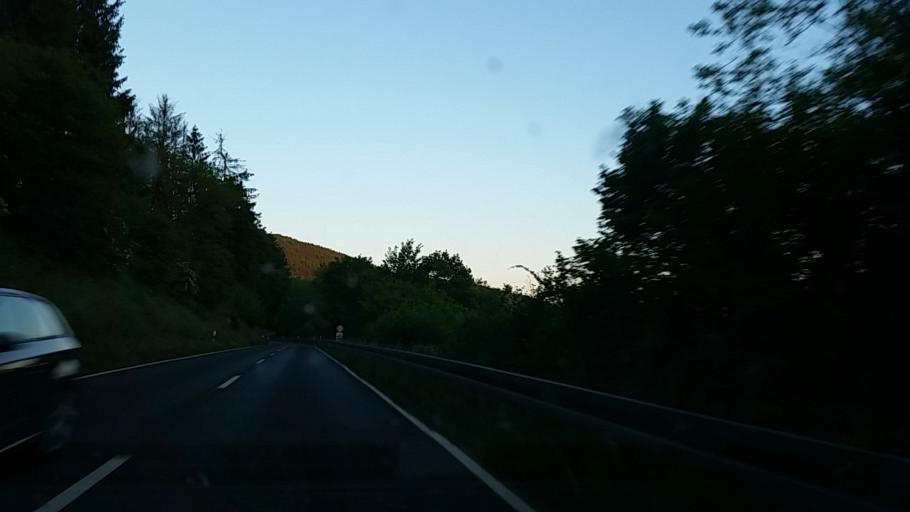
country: DE
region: Bavaria
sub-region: Regierungsbezirk Unterfranken
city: Burgsinn
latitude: 50.1647
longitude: 9.6502
